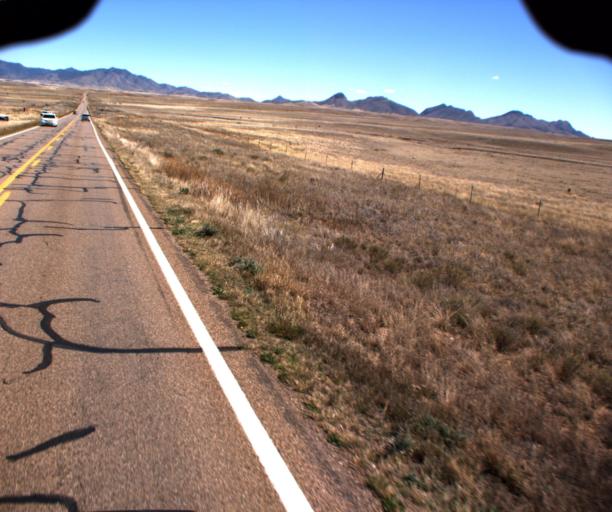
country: US
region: Arizona
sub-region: Cochise County
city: Huachuca City
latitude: 31.6934
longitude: -110.6056
